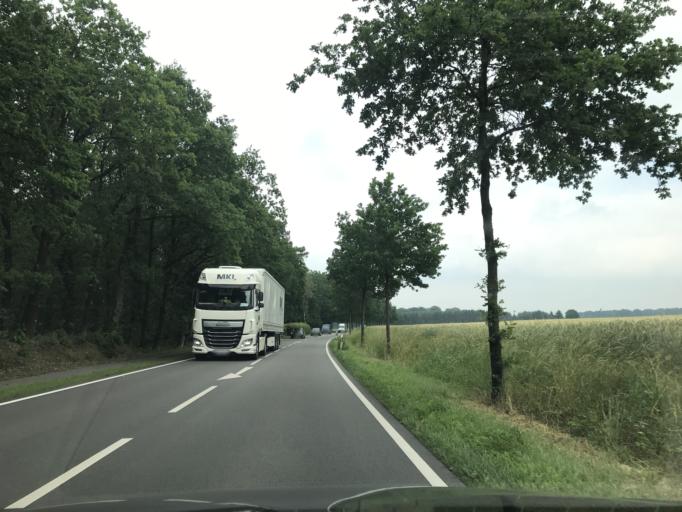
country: DE
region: Lower Saxony
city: Kirchseelte
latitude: 52.9571
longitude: 8.7147
